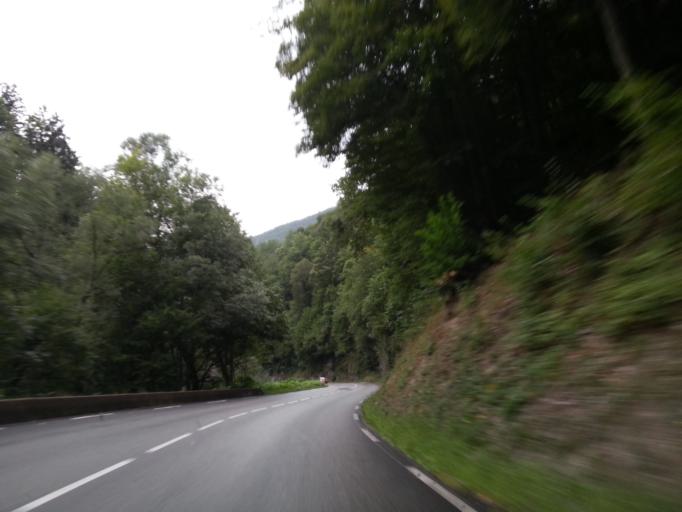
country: FR
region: Rhone-Alpes
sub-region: Departement de la Savoie
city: Marthod
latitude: 45.7163
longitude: 6.4673
